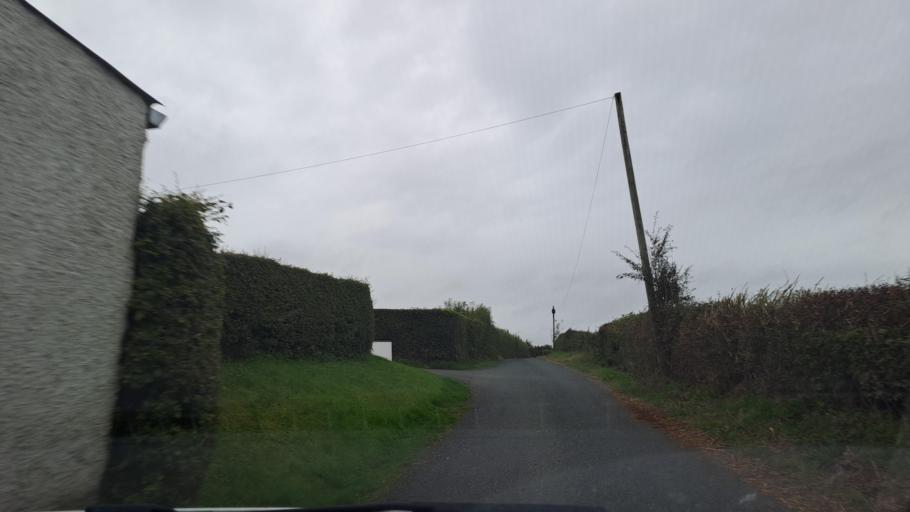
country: IE
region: Ulster
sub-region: County Monaghan
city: Carrickmacross
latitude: 53.9808
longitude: -6.7434
